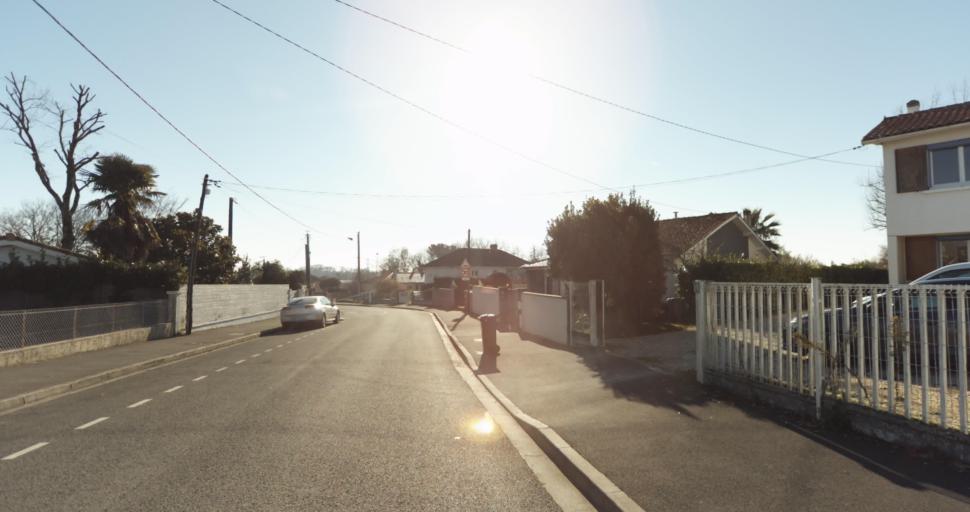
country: FR
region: Aquitaine
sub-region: Departement de la Gironde
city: Carbon-Blanc
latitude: 44.8902
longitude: -0.5108
